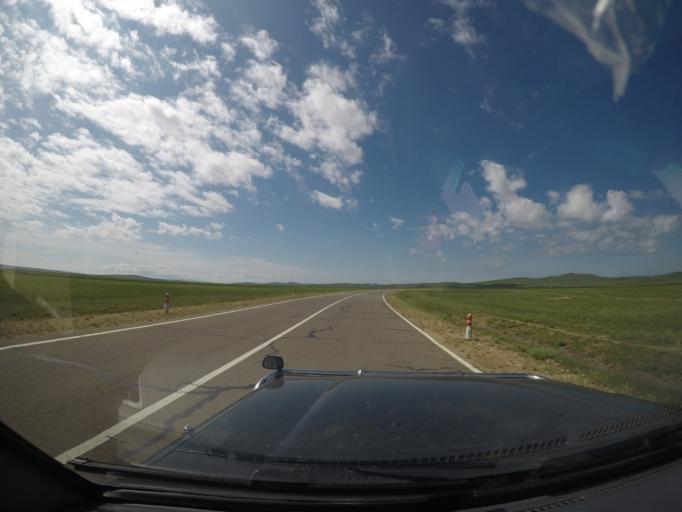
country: MN
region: Suhbaatar
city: Hanhohiy
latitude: 47.3853
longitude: 111.8978
